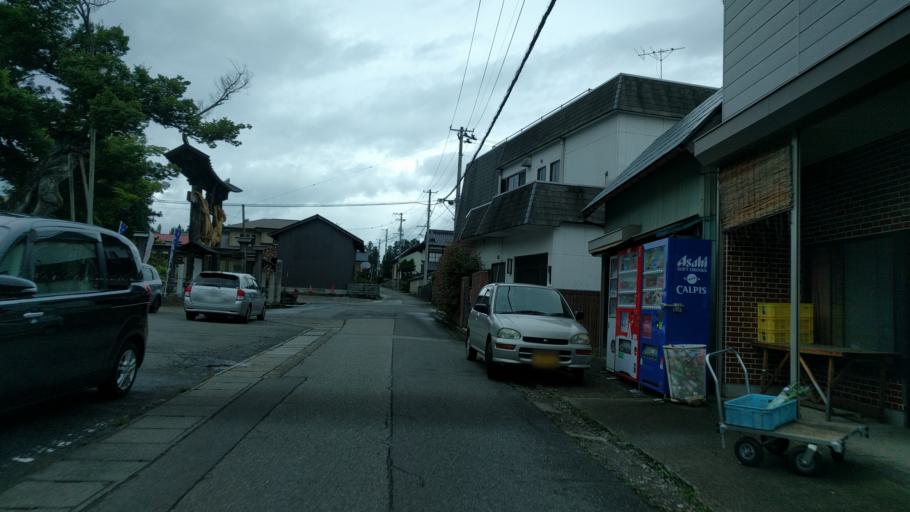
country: JP
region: Fukushima
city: Kitakata
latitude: 37.6185
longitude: 139.8320
